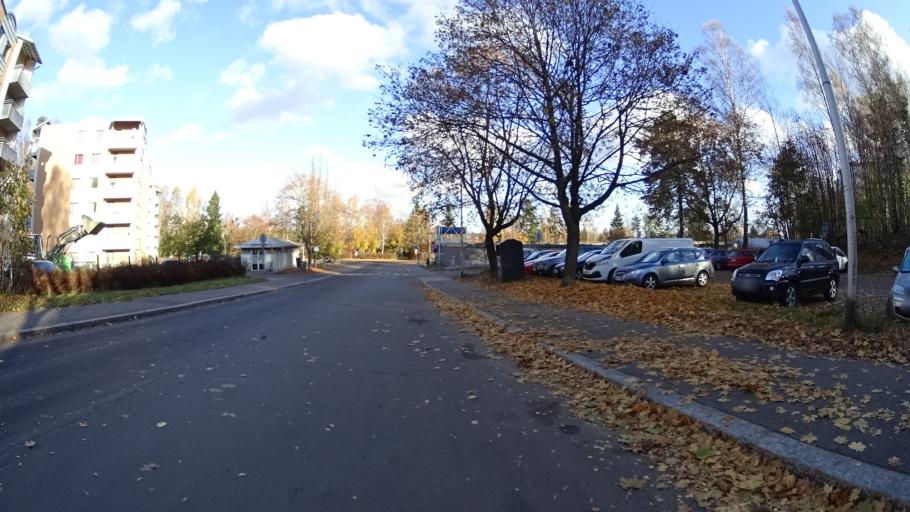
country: FI
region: Uusimaa
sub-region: Helsinki
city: Kilo
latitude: 60.2806
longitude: 24.8439
